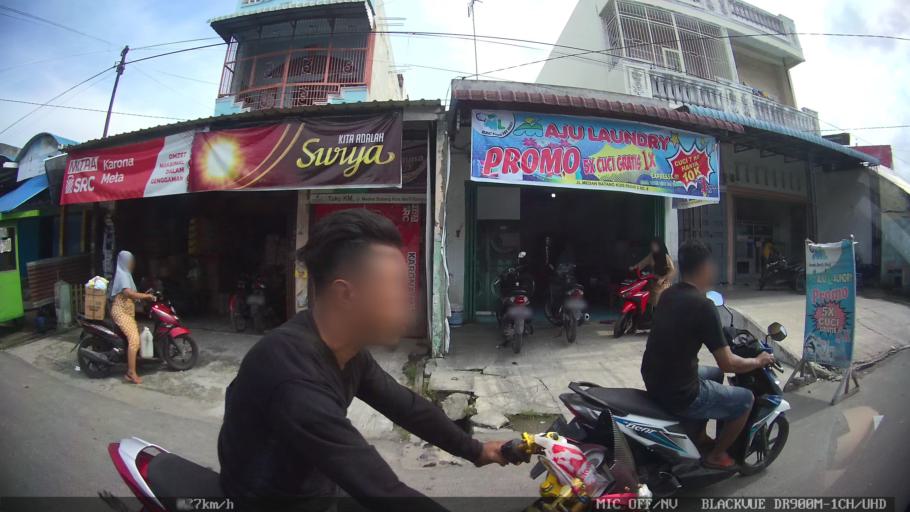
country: ID
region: North Sumatra
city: Medan
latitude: 3.6071
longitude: 98.7584
